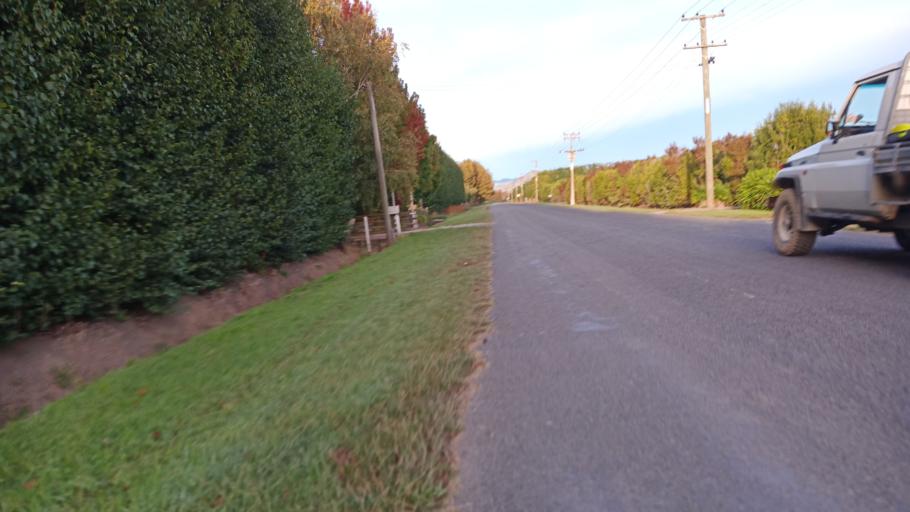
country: NZ
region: Gisborne
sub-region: Gisborne District
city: Gisborne
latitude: -38.6528
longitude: 177.9397
